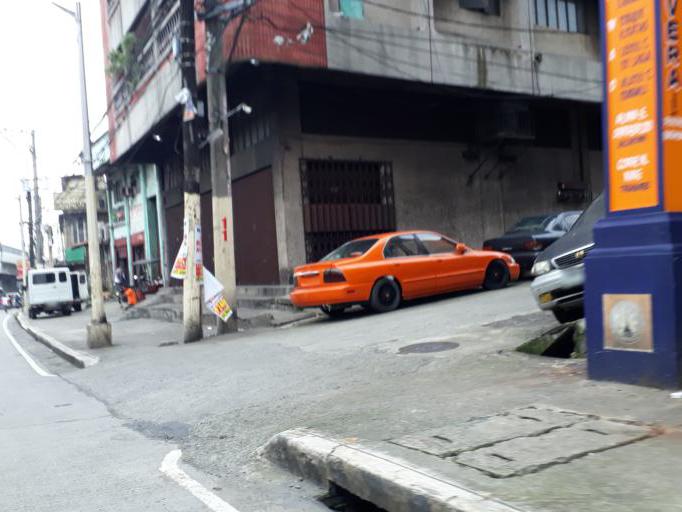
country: PH
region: Metro Manila
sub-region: City of Manila
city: Manila
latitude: 14.6387
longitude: 120.9833
